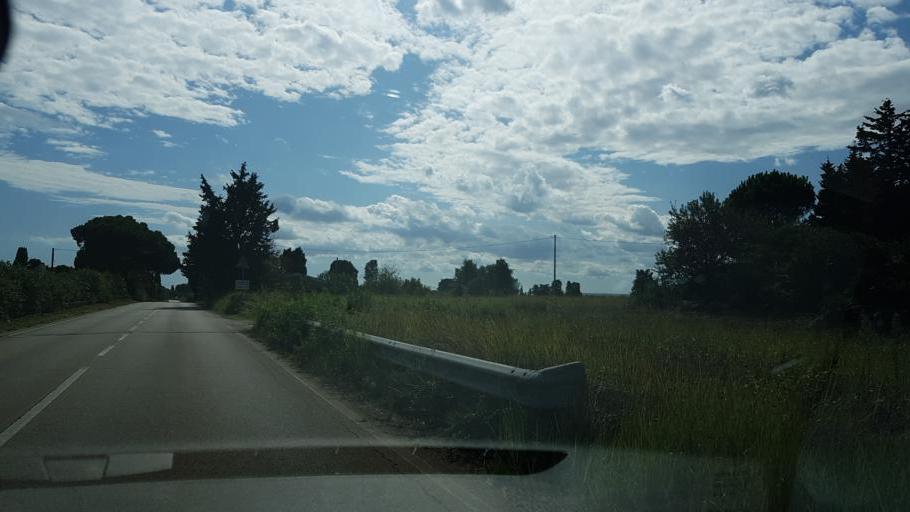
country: IT
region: Apulia
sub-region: Provincia di Lecce
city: Borgagne
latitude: 40.2362
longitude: 18.4440
